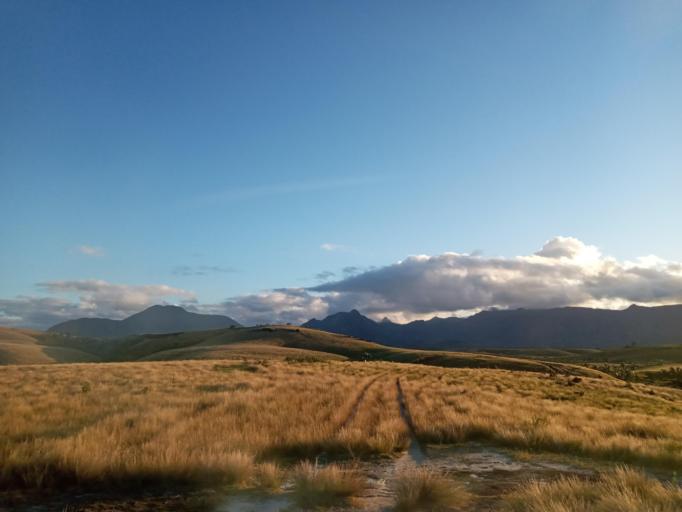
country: MG
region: Anosy
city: Fort Dauphin
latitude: -24.5119
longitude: 47.2552
